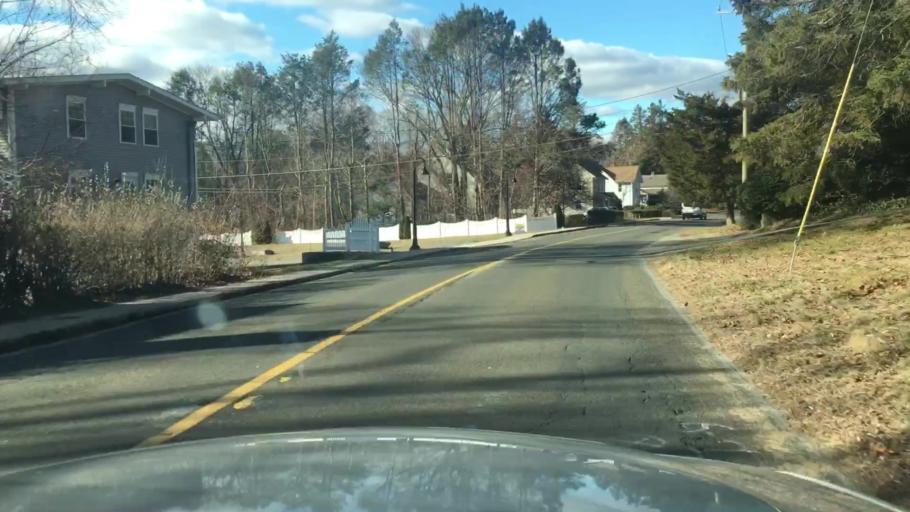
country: US
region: Connecticut
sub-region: Middlesex County
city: Deep River Center
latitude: 41.3821
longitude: -72.4305
